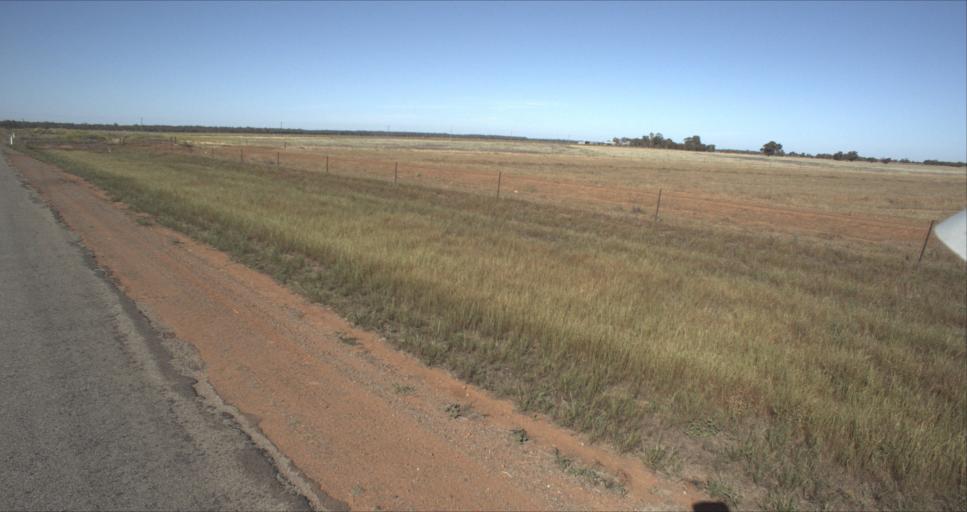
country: AU
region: New South Wales
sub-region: Leeton
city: Leeton
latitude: -34.5806
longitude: 146.3089
